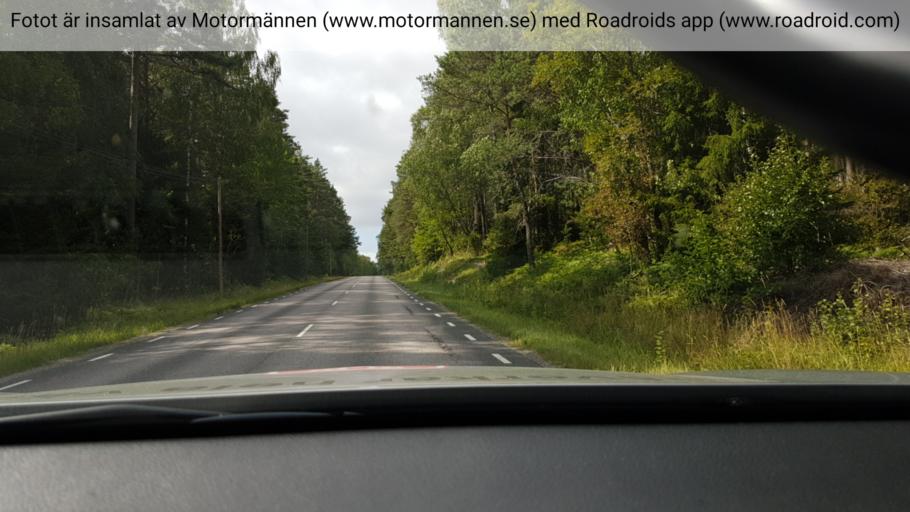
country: SE
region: Stockholm
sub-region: Norrtalje Kommun
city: Rimbo
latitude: 59.7066
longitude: 18.4176
